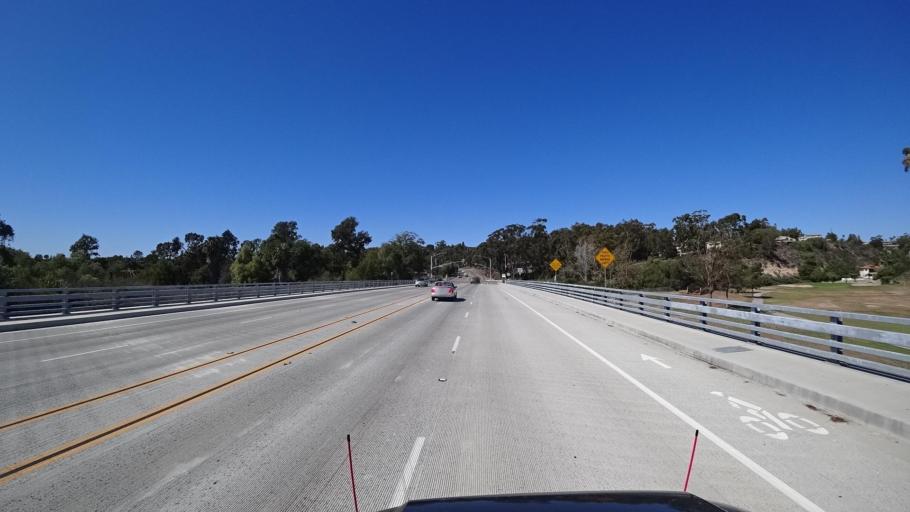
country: US
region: California
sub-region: San Diego County
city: Bonita
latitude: 32.6592
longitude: -117.0425
